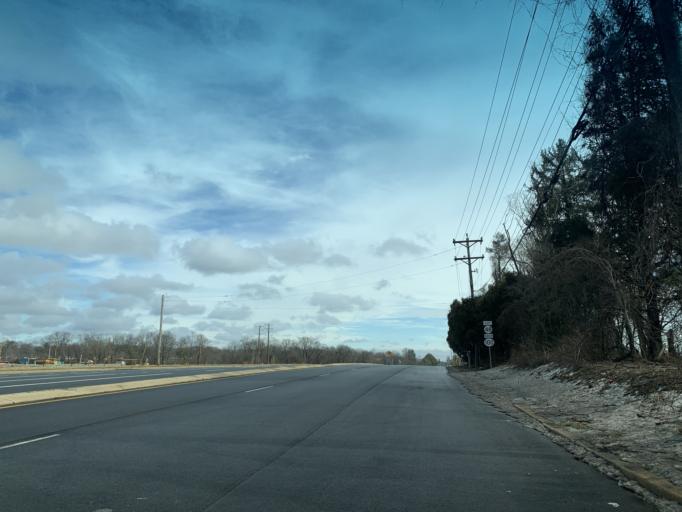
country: US
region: Delaware
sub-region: New Castle County
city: Elsmere
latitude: 39.7586
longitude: -75.6040
